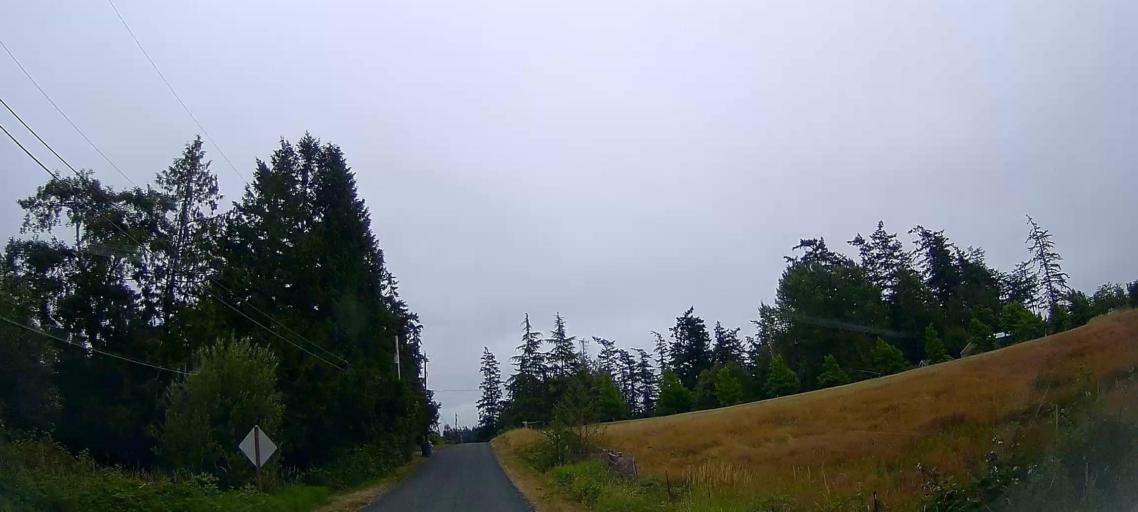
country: US
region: Washington
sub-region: Skagit County
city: Anacortes
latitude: 48.4335
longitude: -122.6154
